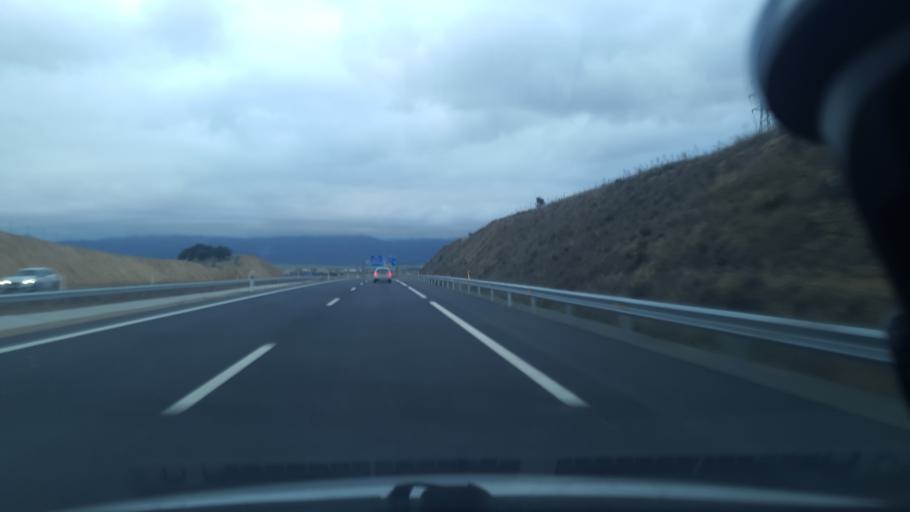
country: ES
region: Castille and Leon
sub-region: Provincia de Segovia
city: Segovia
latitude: 40.9207
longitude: -4.1332
